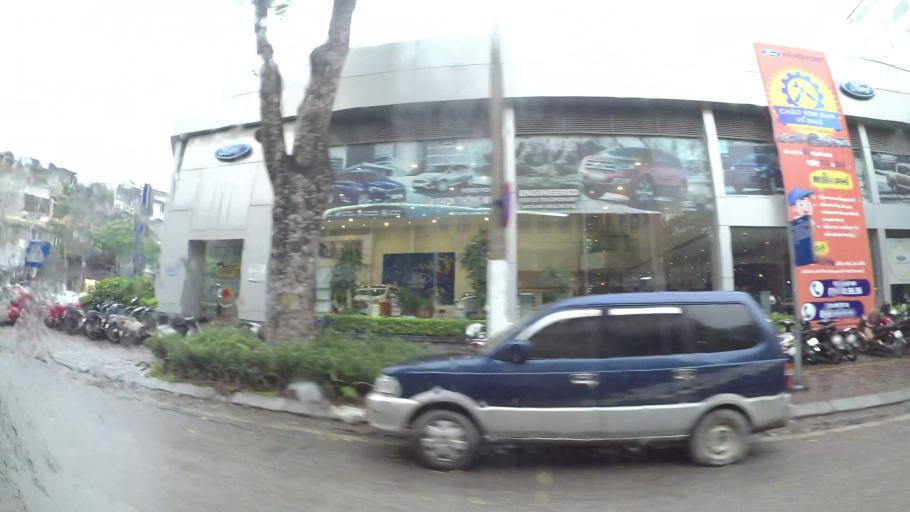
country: VN
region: Ha Noi
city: Hai BaTrung
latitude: 21.0141
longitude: 105.8534
